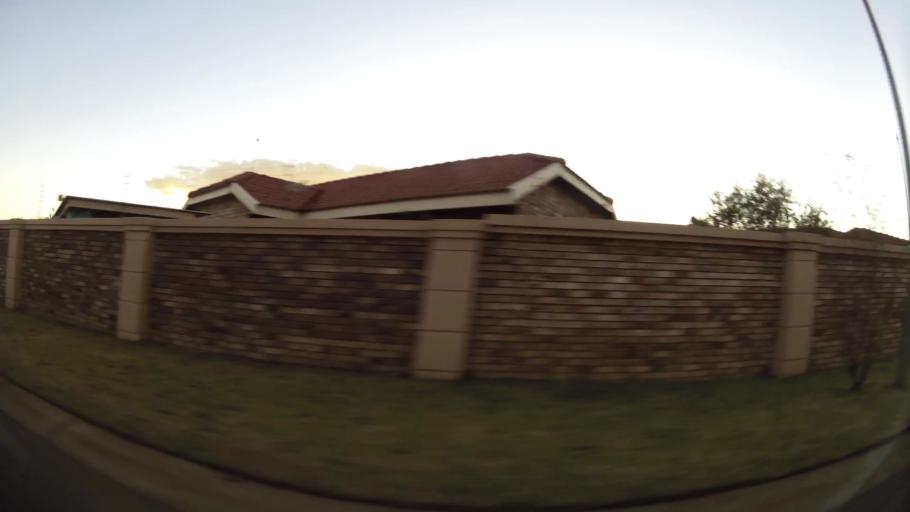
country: ZA
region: North-West
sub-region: Dr Kenneth Kaunda District Municipality
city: Potchefstroom
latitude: -26.7256
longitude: 27.1141
